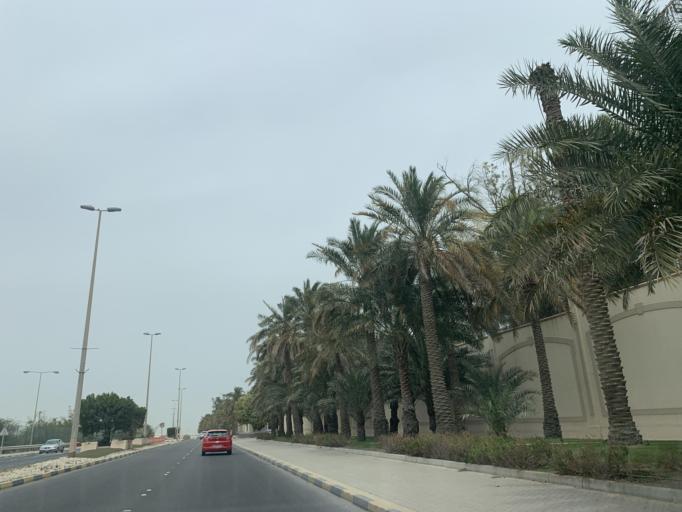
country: BH
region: Northern
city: Ar Rifa'
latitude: 26.1376
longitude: 50.5430
